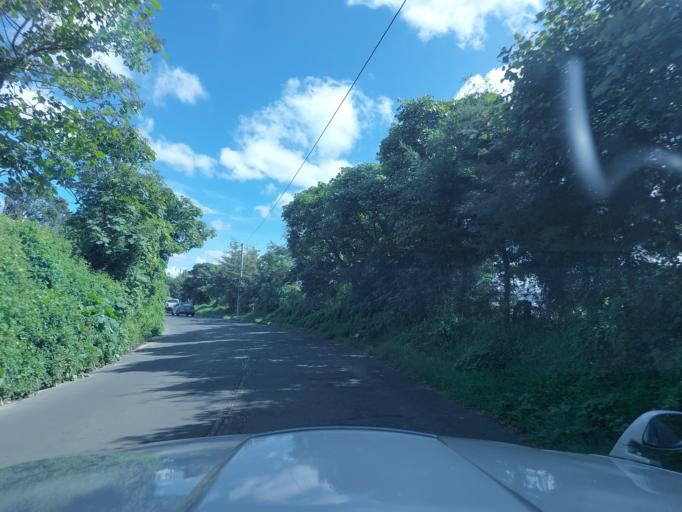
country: GT
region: Chimaltenango
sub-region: Municipio de Zaragoza
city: Zaragoza
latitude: 14.6588
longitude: -90.8973
